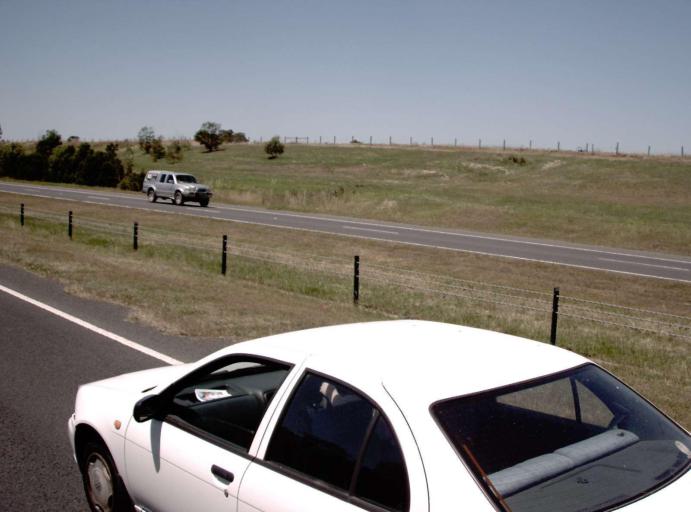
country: AU
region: Victoria
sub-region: Cardinia
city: Officer South
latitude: -38.0665
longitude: 145.3771
